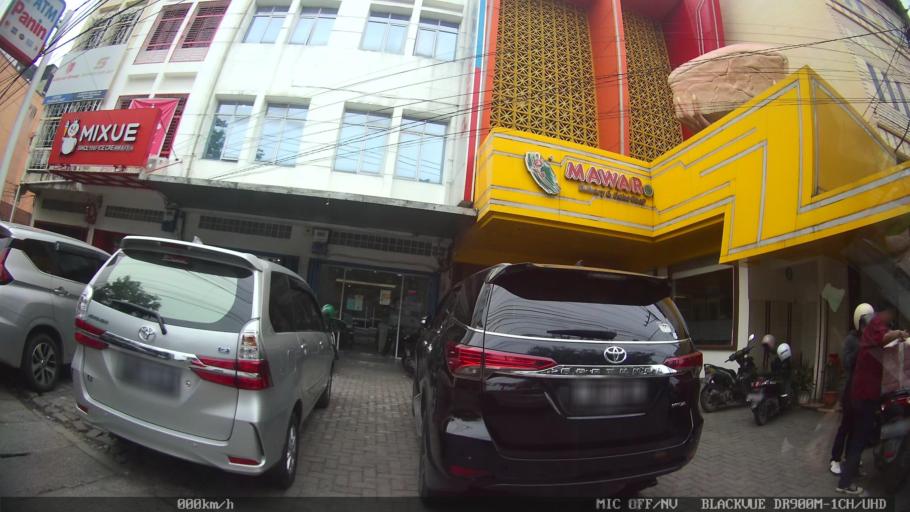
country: ID
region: North Sumatra
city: Deli Tua
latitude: 3.5470
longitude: 98.6876
